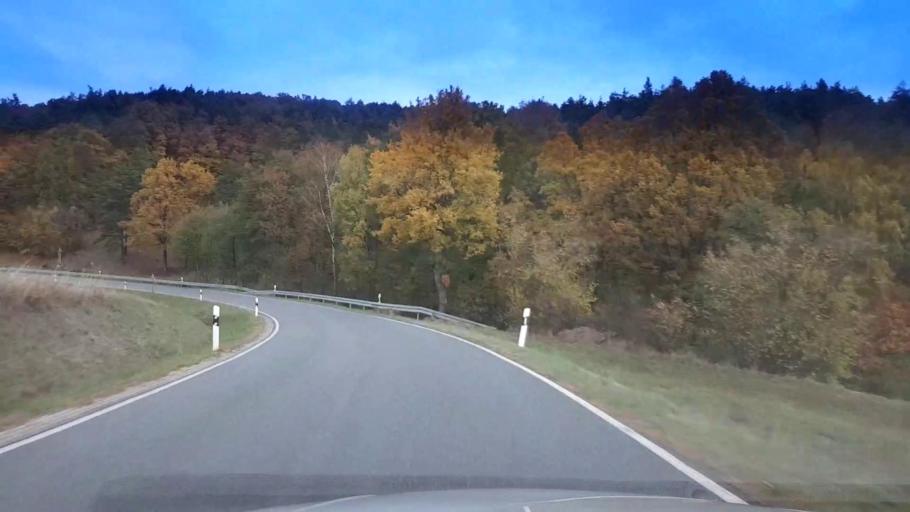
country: DE
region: Bavaria
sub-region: Regierungsbezirk Unterfranken
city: Stettfeld
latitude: 49.9426
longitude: 10.7051
